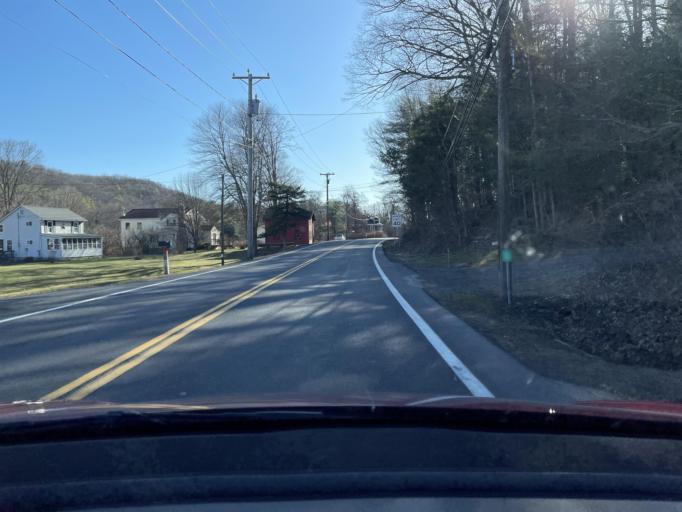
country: US
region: New York
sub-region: Ulster County
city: Saugerties
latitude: 42.0820
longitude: -73.9999
